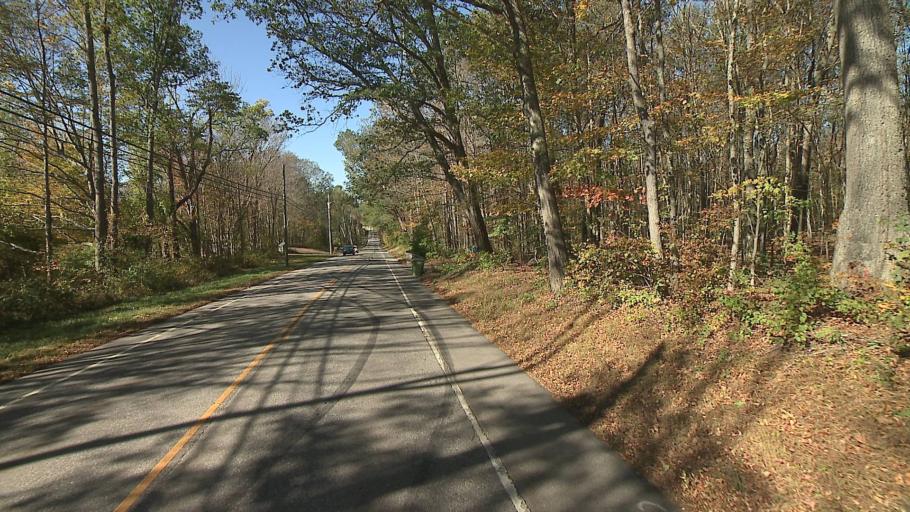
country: US
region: Connecticut
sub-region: Tolland County
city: Hebron
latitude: 41.6473
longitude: -72.4131
